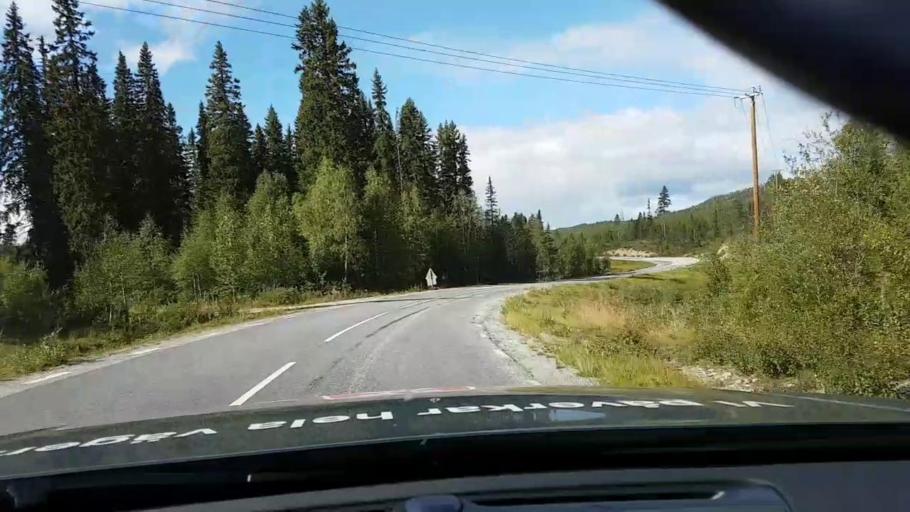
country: SE
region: Vaesterbotten
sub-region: Asele Kommun
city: Asele
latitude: 63.8244
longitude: 17.4770
